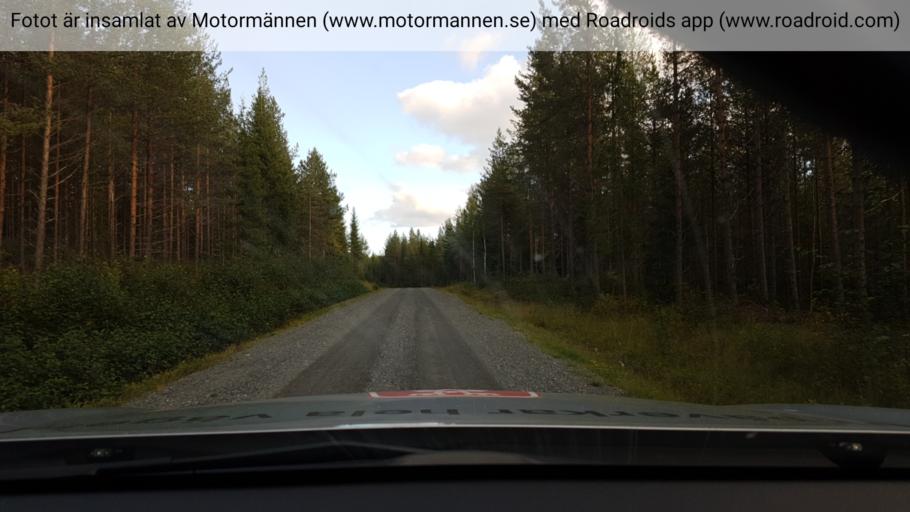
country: SE
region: Vaesterbotten
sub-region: Norsjo Kommun
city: Norsjoe
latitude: 64.9566
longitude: 19.2254
